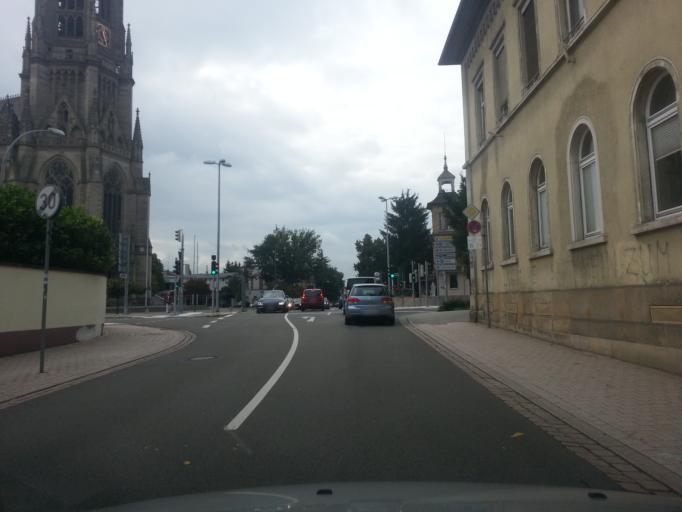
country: DE
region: Rheinland-Pfalz
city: Speyer
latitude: 49.3159
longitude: 8.4296
